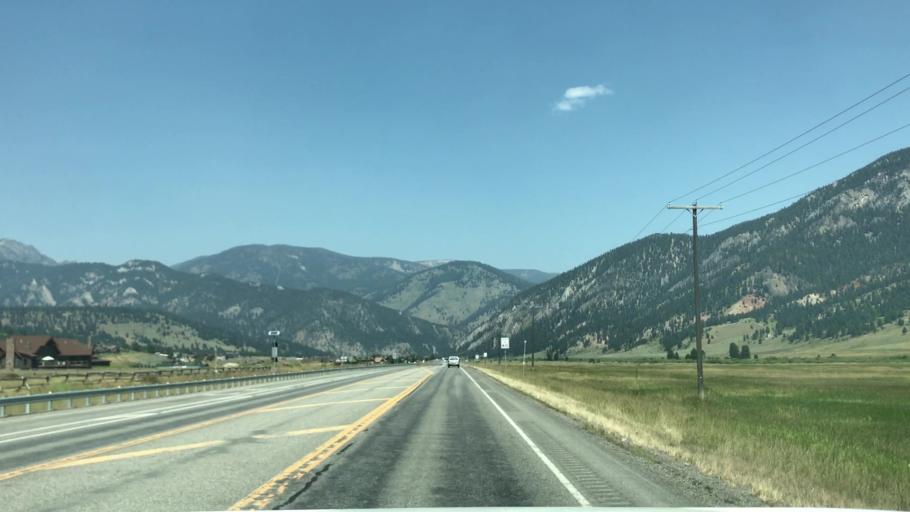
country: US
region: Montana
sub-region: Gallatin County
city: Big Sky
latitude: 45.2323
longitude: -111.2508
